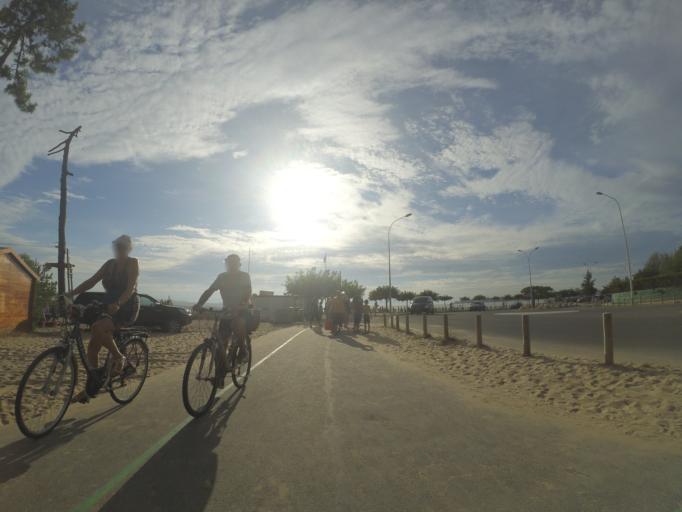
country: FR
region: Poitou-Charentes
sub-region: Departement de la Charente-Maritime
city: Saint-Georges-de-Didonne
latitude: 45.5893
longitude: -0.9886
